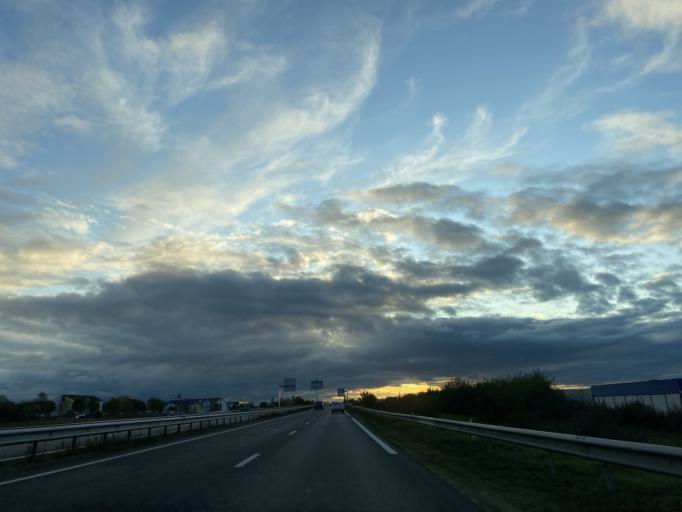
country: FR
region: Centre
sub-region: Departement du Cher
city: La Chapelle-Saint-Ursin
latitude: 47.0500
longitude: 2.3444
